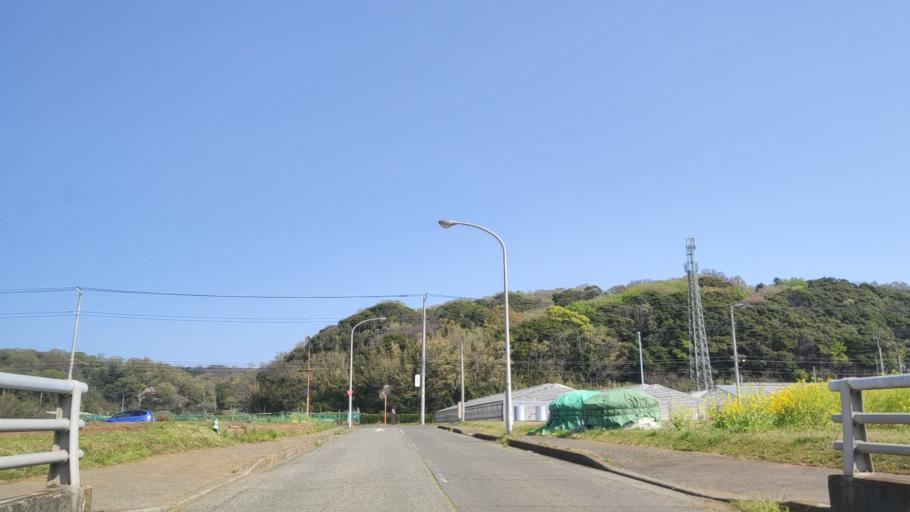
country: JP
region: Kanagawa
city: Oiso
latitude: 35.3087
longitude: 139.2967
